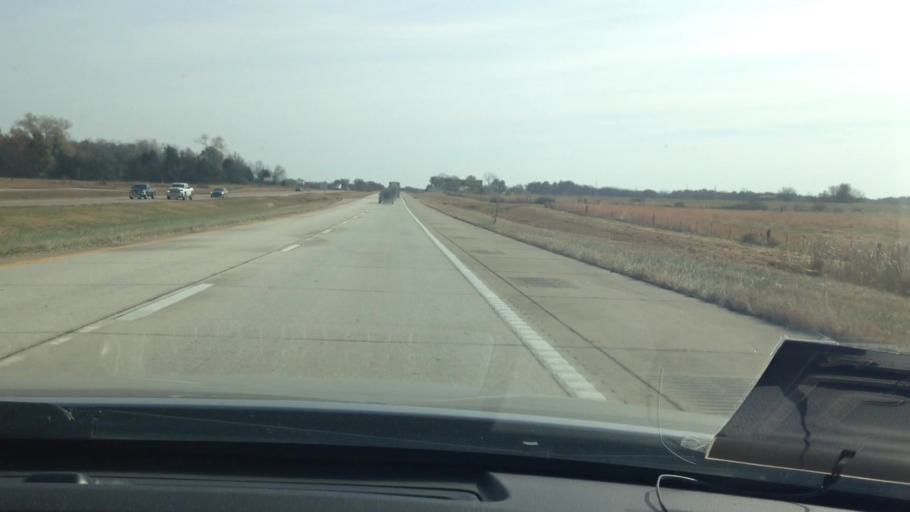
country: US
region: Missouri
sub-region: Henry County
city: Clinton
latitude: 38.4073
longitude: -93.8471
